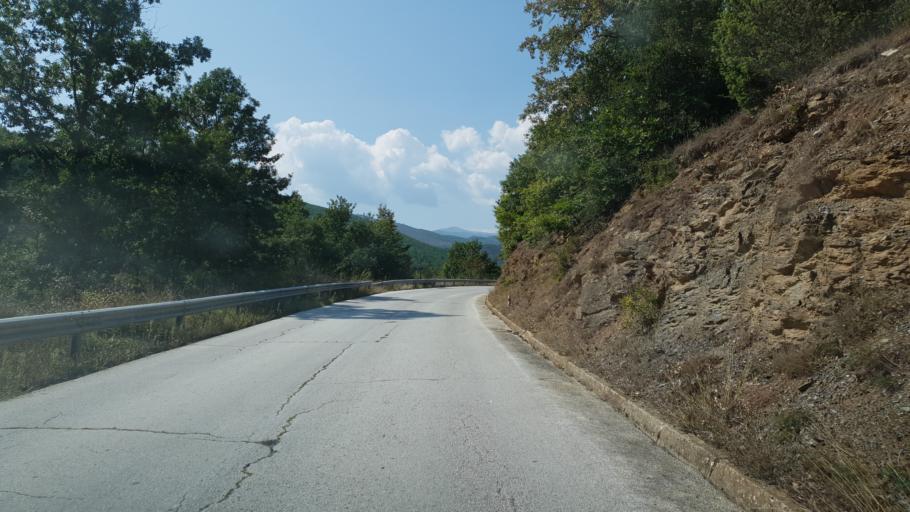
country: MK
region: Makedonski Brod
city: Samokov
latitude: 41.6692
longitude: 21.2382
